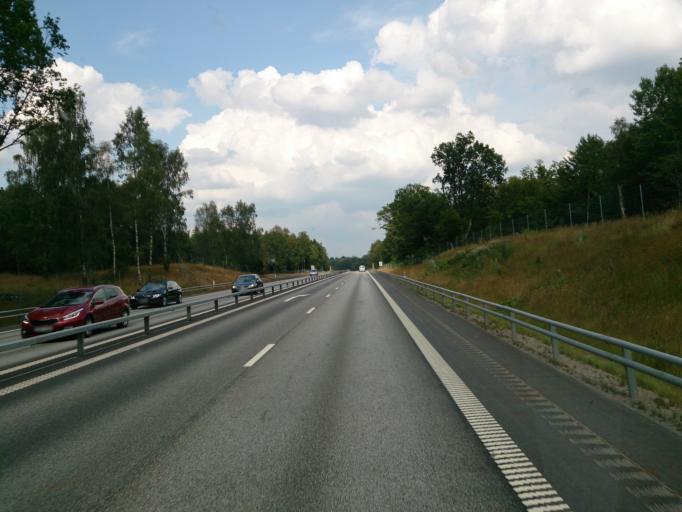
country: SE
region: Skane
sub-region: Horby Kommun
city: Hoerby
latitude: 55.9187
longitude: 13.7824
